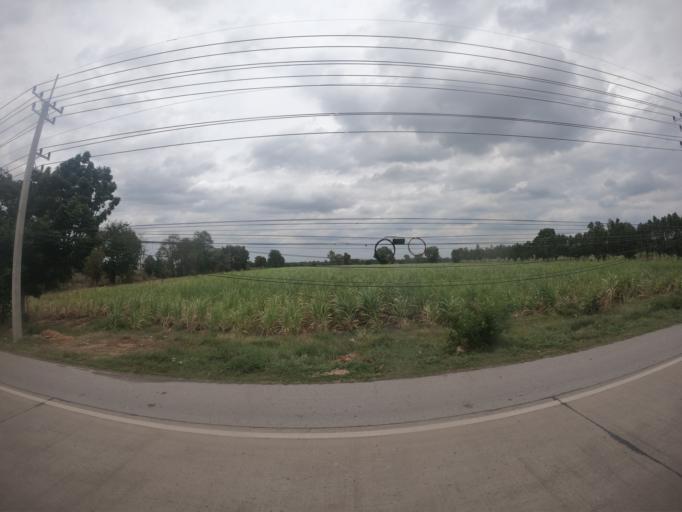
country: TH
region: Nakhon Ratchasima
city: Chok Chai
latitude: 14.8080
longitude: 102.1744
